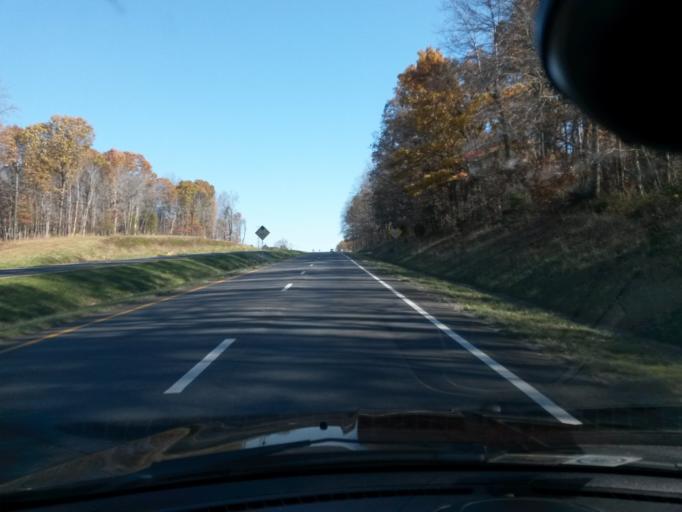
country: US
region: Virginia
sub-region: Campbell County
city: Timberlake
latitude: 37.3043
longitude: -79.3187
